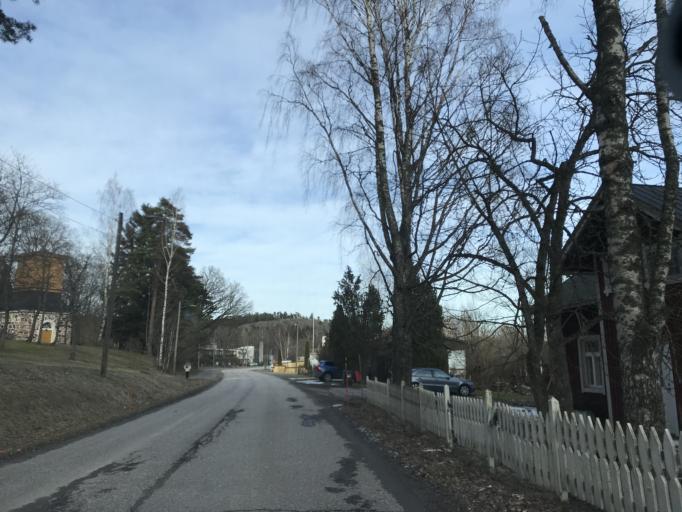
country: FI
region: Uusimaa
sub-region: Raaseporin
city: Pohja
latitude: 60.0947
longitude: 23.5216
